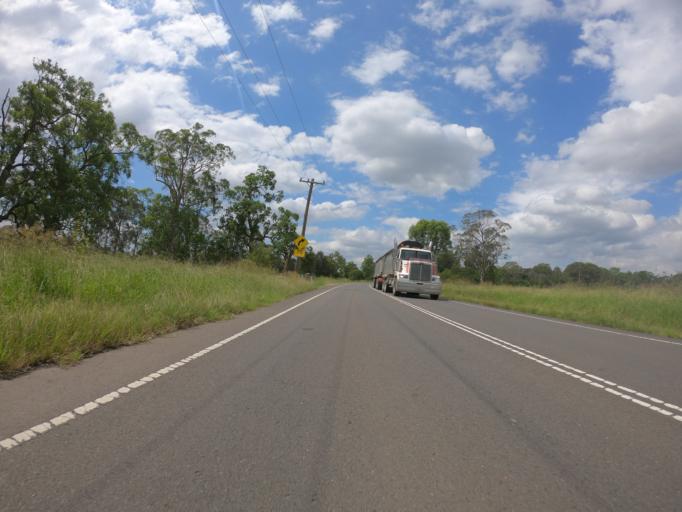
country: AU
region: New South Wales
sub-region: Penrith Municipality
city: Kingswood Park
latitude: -33.8061
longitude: 150.7655
